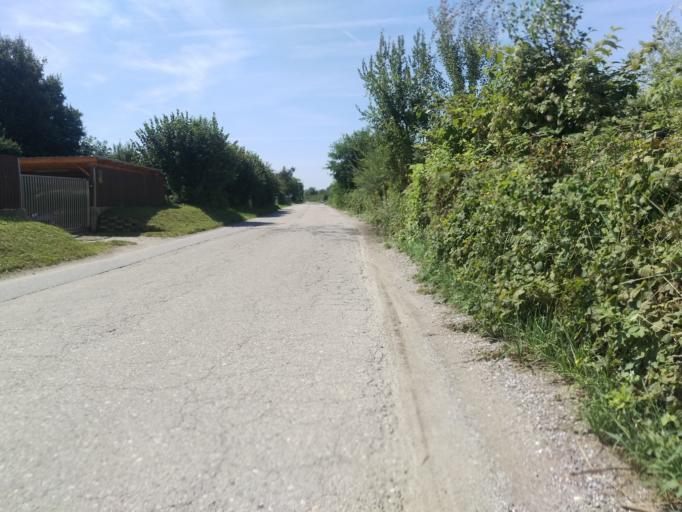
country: AT
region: Styria
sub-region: Politischer Bezirk Graz-Umgebung
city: Seiersberg
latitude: 46.9935
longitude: 15.4223
